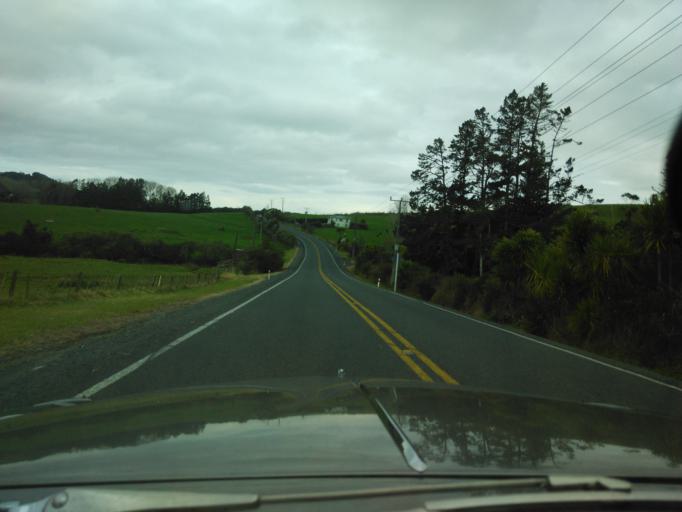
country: NZ
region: Auckland
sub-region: Auckland
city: Parakai
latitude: -36.6354
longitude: 174.5324
